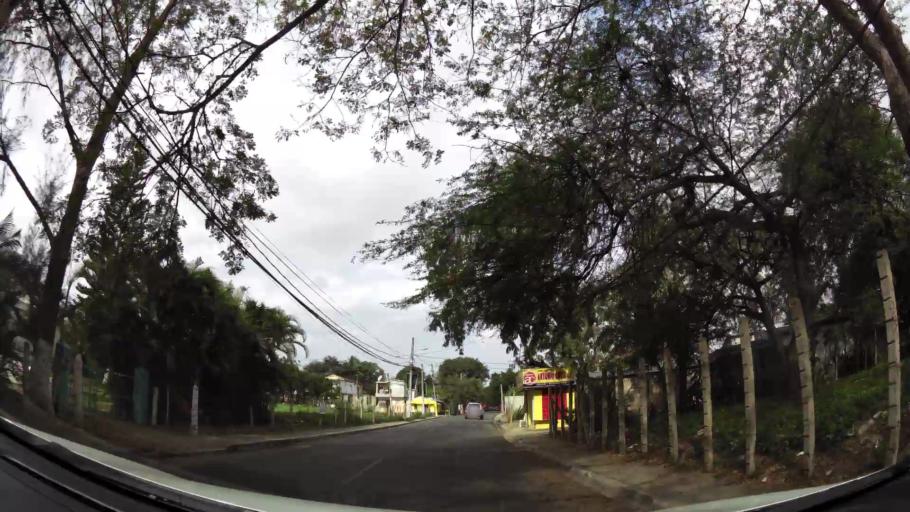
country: DO
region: Santiago
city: Santiago de los Caballeros
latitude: 19.4264
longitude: -70.6574
